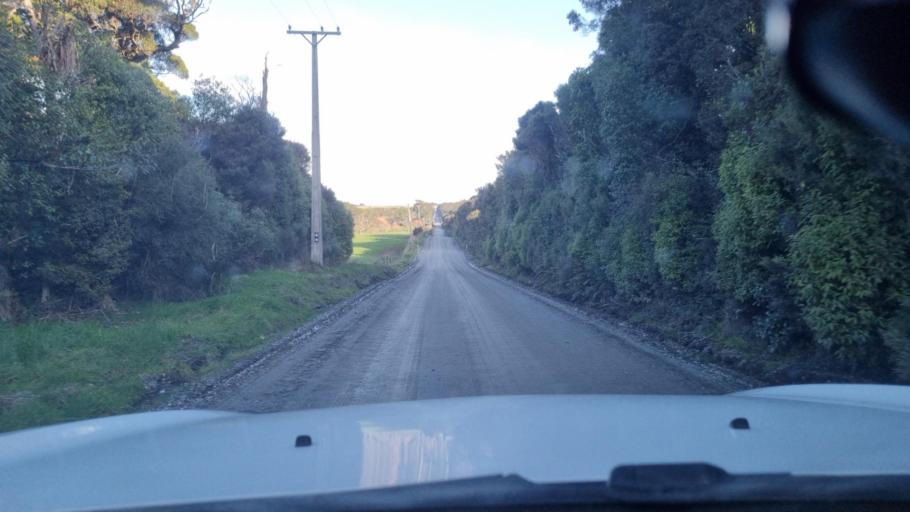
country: NZ
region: Southland
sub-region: Invercargill City
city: Bluff
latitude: -46.5273
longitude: 168.2696
